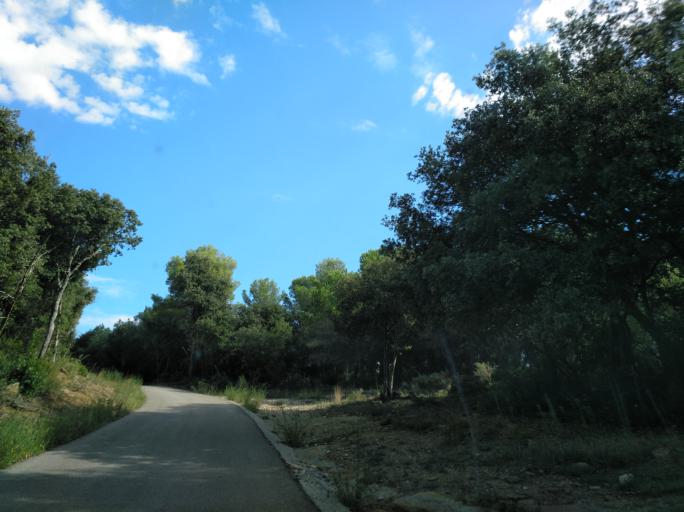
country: ES
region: Catalonia
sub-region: Provincia de Girona
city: la Cellera de Ter
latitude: 42.0203
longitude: 2.6296
